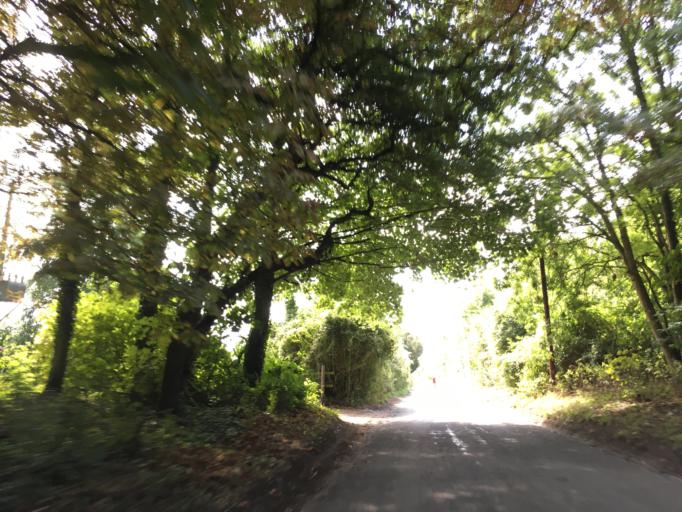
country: GB
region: England
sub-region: Hampshire
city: Andover
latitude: 51.1869
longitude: -1.3768
